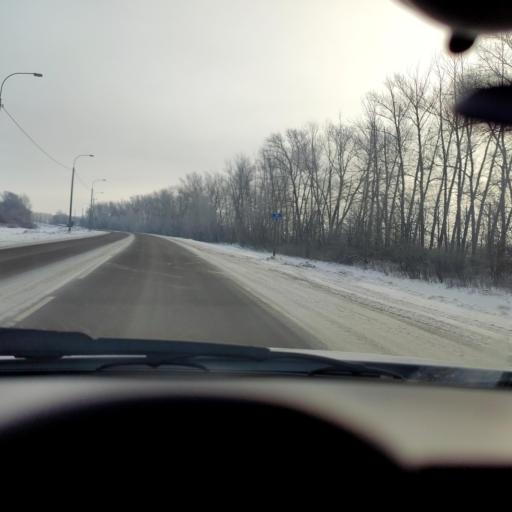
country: RU
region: Kursk
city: Kirovskiy
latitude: 51.6770
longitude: 36.5918
